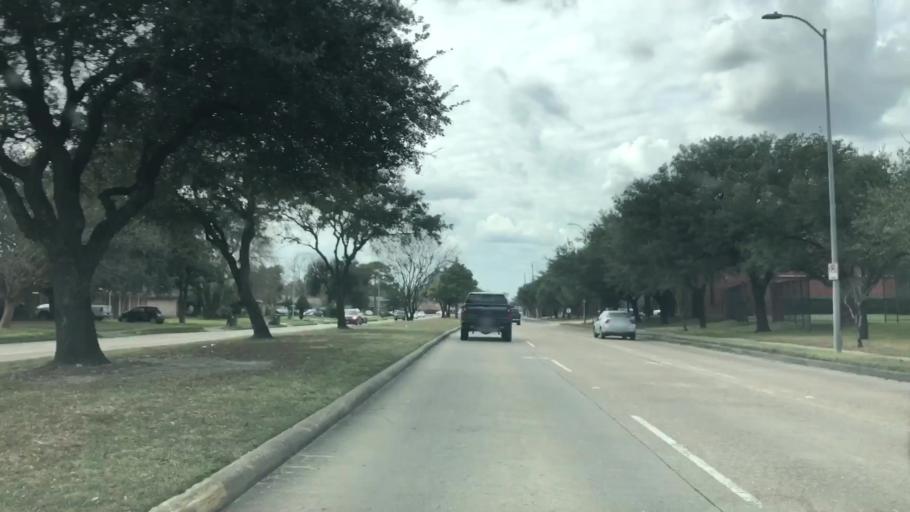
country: US
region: Texas
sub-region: Harris County
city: Bellaire
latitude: 29.6912
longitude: -95.5155
